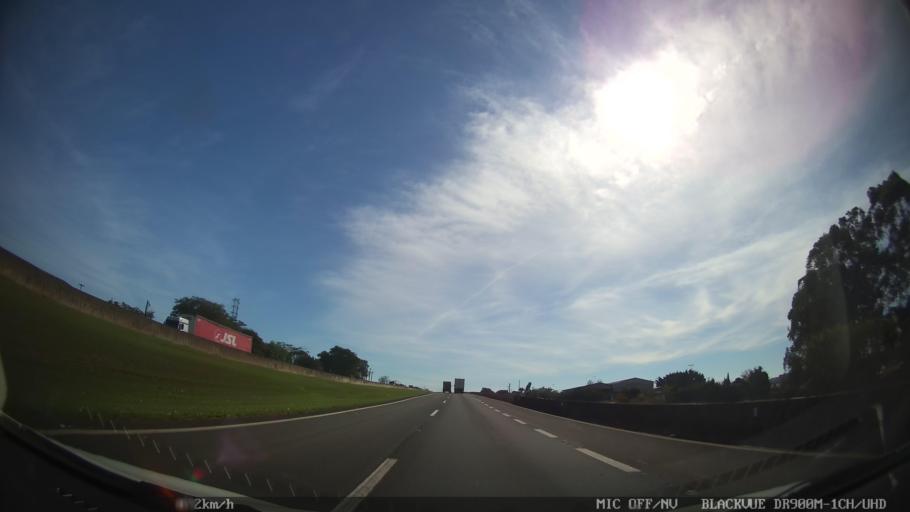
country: BR
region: Sao Paulo
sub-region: Leme
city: Leme
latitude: -22.1867
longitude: -47.3982
